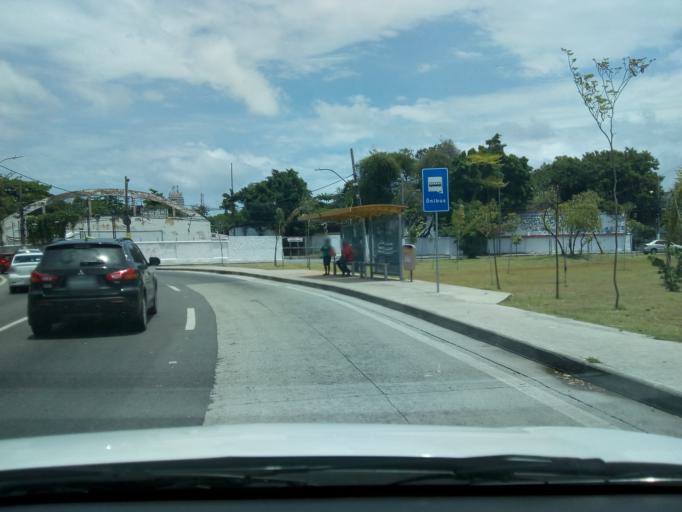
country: BR
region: Rio de Janeiro
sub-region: Niteroi
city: Niteroi
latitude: -22.8832
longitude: -43.1159
